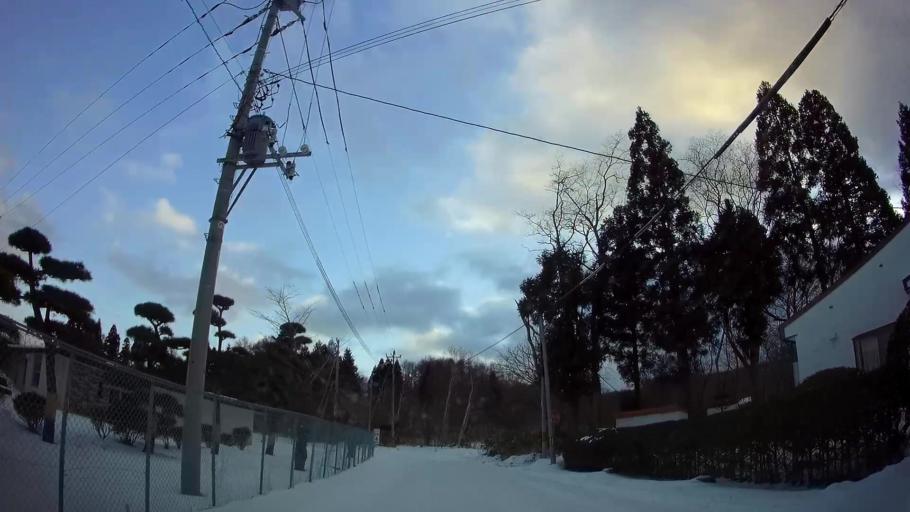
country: JP
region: Hokkaido
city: Nanae
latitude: 42.0231
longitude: 140.8329
